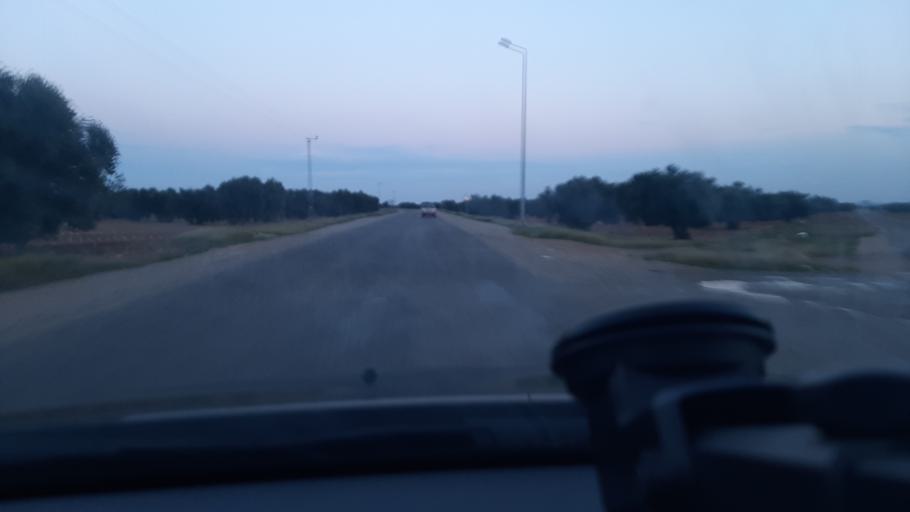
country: TN
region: Al Mahdiyah
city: Shurban
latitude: 35.0189
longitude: 10.4619
